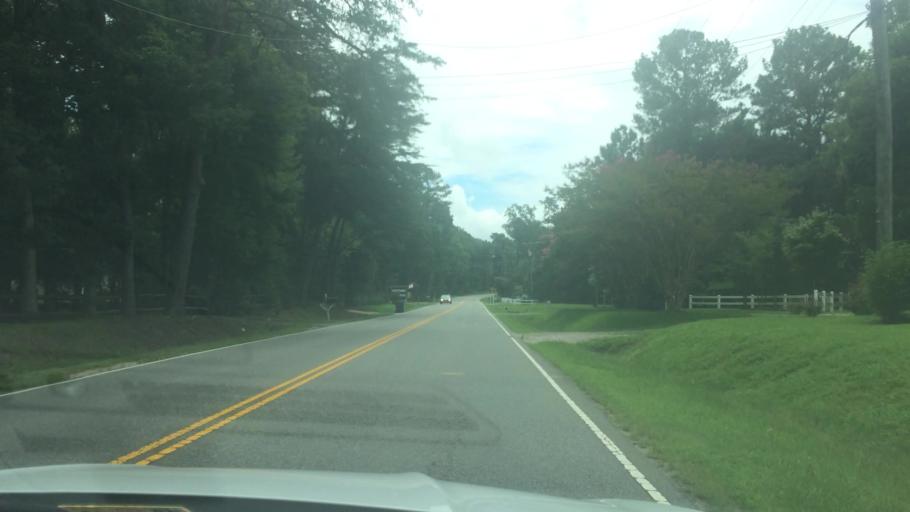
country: US
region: Virginia
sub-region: James City County
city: Williamsburg
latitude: 37.2478
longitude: -76.7627
